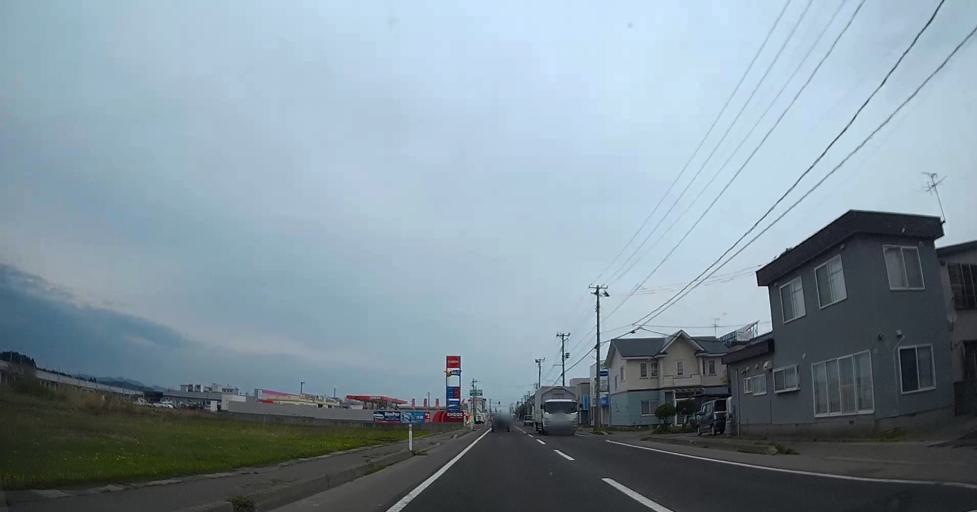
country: JP
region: Aomori
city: Aomori Shi
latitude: 40.8557
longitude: 140.6814
